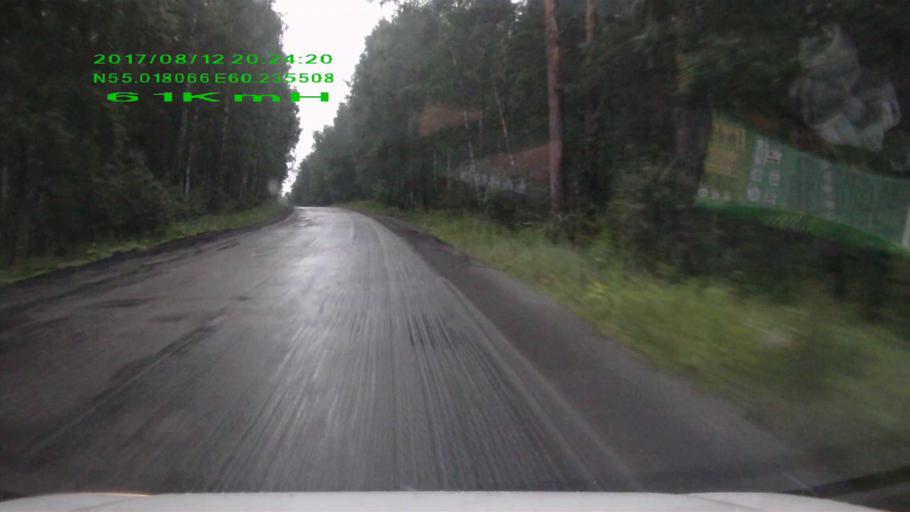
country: RU
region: Chelyabinsk
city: Miass
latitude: 55.0179
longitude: 60.2352
